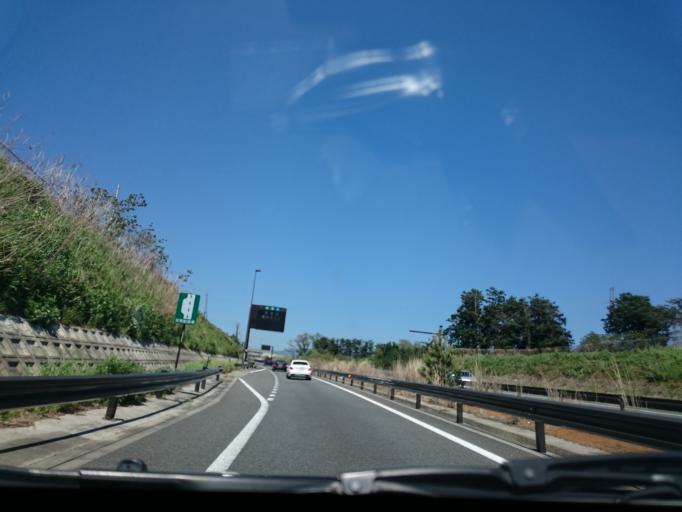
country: JP
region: Shizuoka
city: Numazu
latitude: 35.1434
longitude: 138.8717
